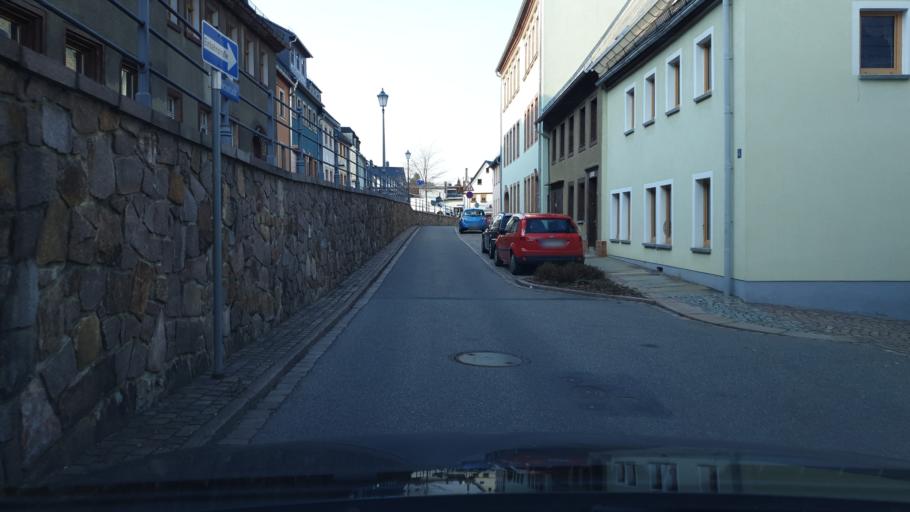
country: DE
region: Saxony
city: Mittweida
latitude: 50.9844
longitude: 12.9787
